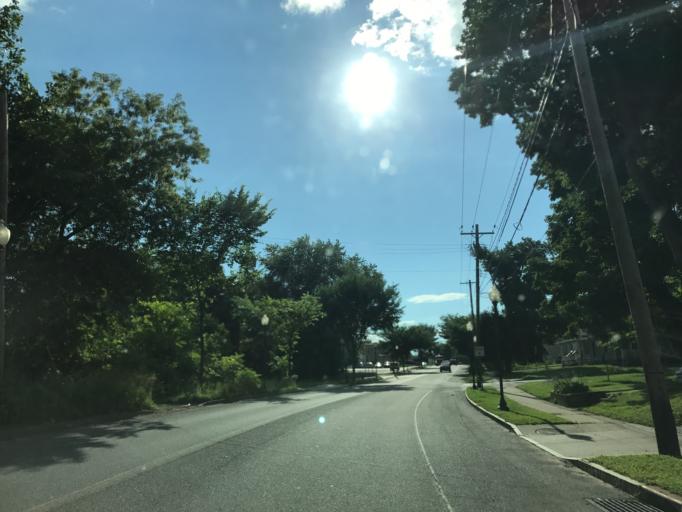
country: US
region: New York
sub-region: Saratoga County
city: South Glens Falls
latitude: 43.3099
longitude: -73.6243
